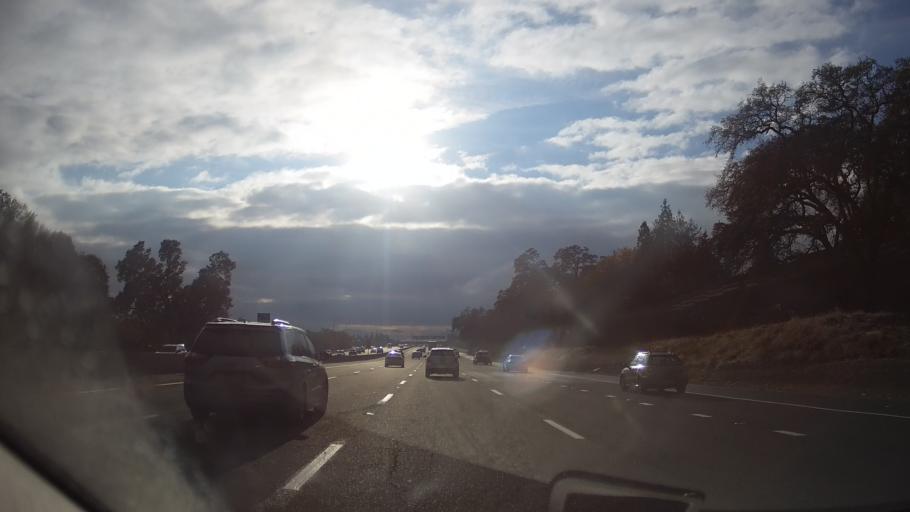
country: US
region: California
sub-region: Placer County
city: Rocklin
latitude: 38.7759
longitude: -121.2393
